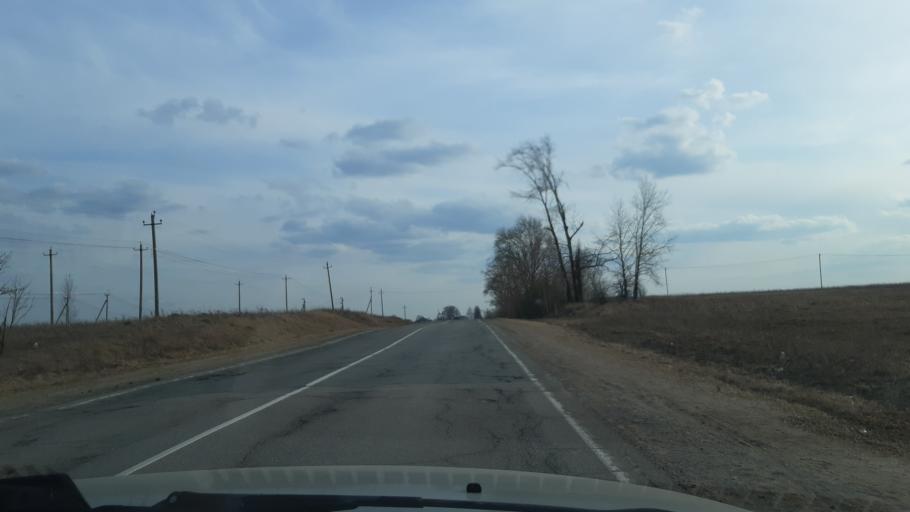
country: RU
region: Vladimir
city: Nikologory
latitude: 56.1571
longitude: 41.9959
